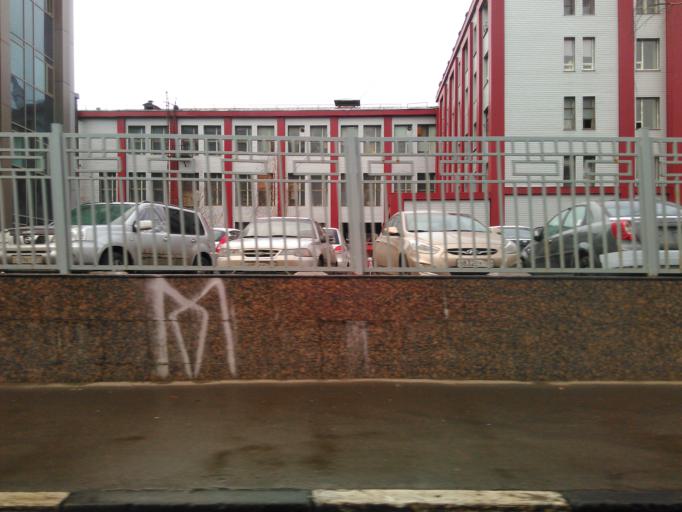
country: RU
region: Moscow
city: Zamoskvorech'ye
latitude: 55.7192
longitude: 37.6346
